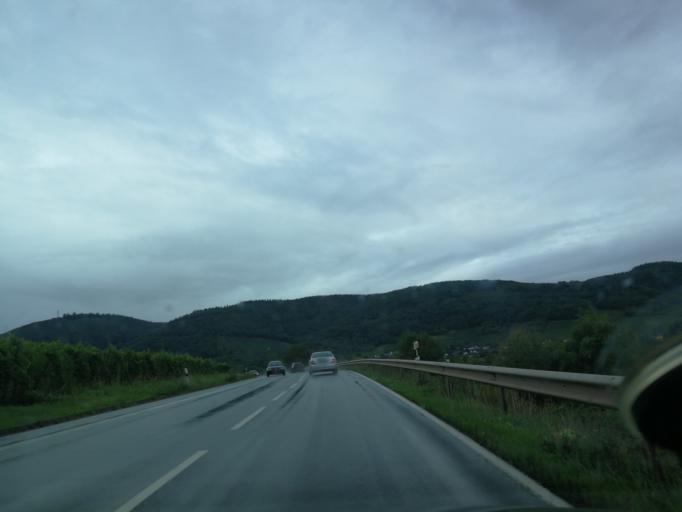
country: DE
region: Rheinland-Pfalz
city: Lieser
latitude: 49.9131
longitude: 7.0418
